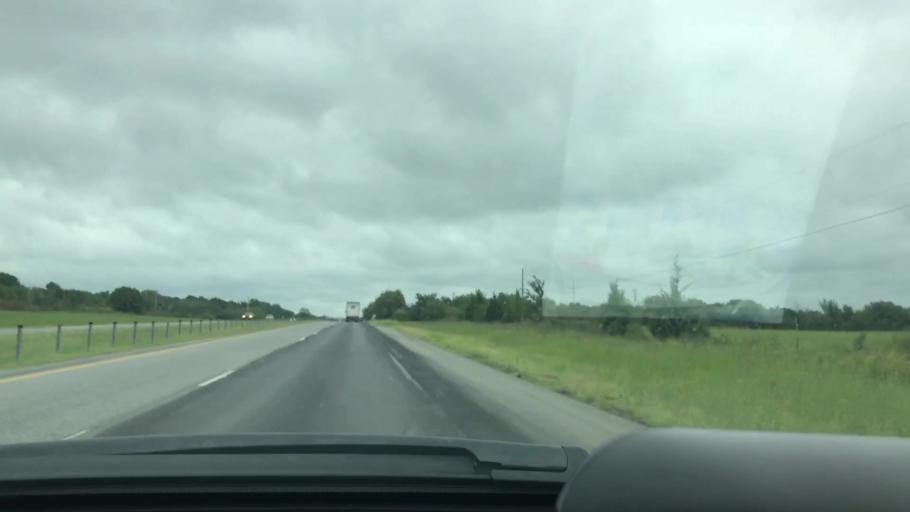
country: US
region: Oklahoma
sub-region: Pittsburg County
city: McAlester
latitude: 34.7971
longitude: -95.8706
